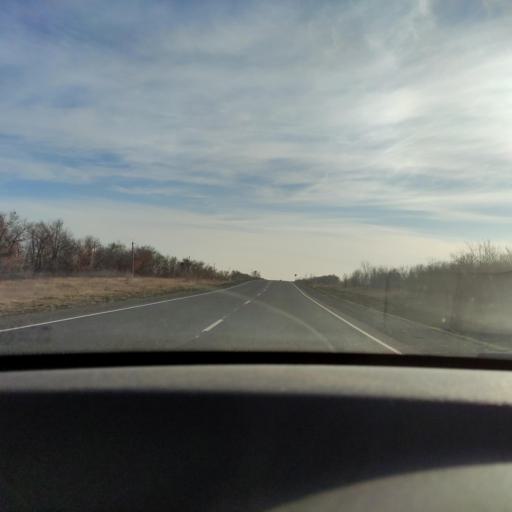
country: RU
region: Samara
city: Krasnoarmeyskoye
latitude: 52.8121
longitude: 50.0114
